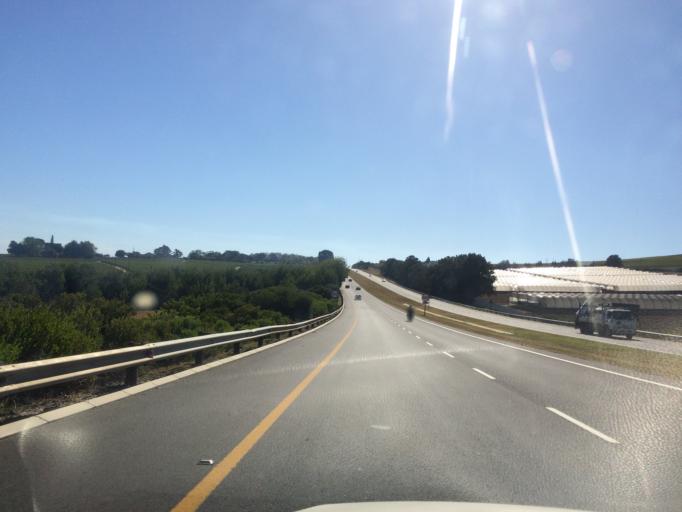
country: ZA
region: Western Cape
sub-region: City of Cape Town
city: Kraaifontein
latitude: -33.9631
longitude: 18.7426
